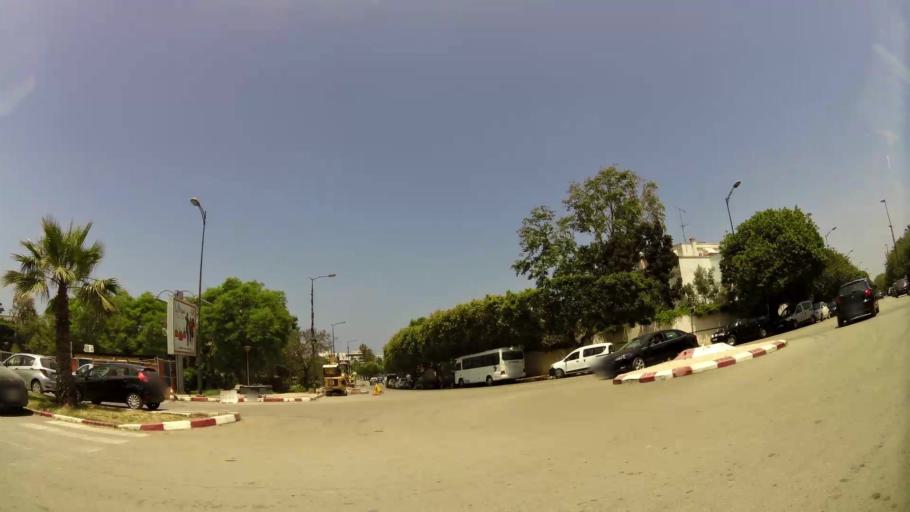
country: MA
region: Rabat-Sale-Zemmour-Zaer
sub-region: Rabat
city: Rabat
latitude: 34.0137
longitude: -6.8257
